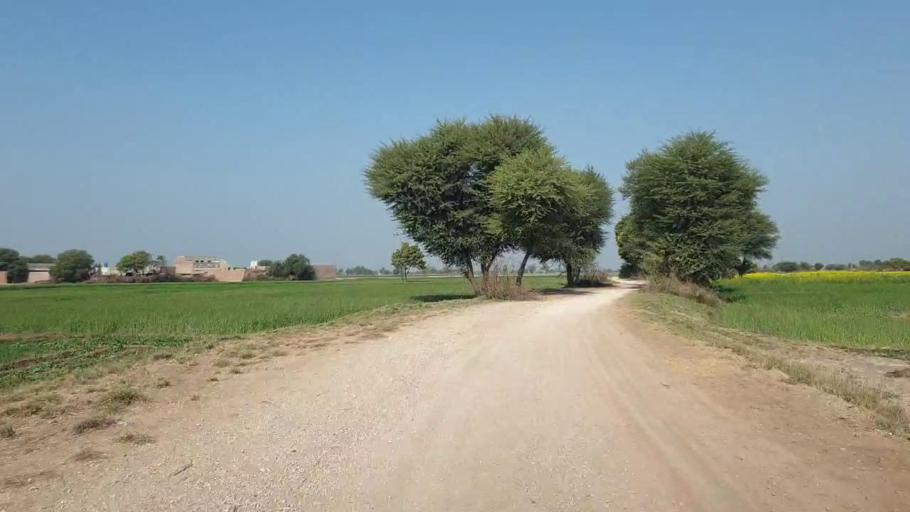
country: PK
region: Sindh
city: Hala
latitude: 25.9237
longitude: 68.4065
